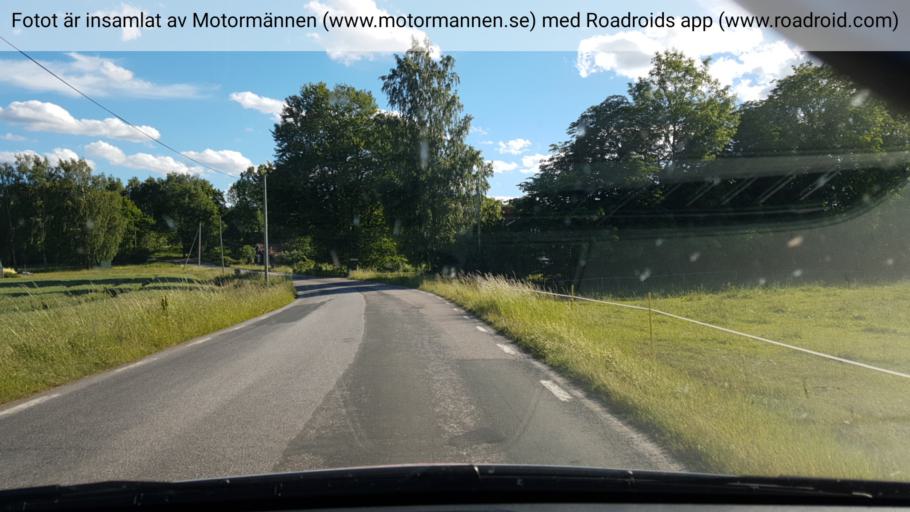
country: SE
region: Vaestra Goetaland
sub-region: Skovde Kommun
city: Stopen
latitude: 58.4903
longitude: 13.8697
